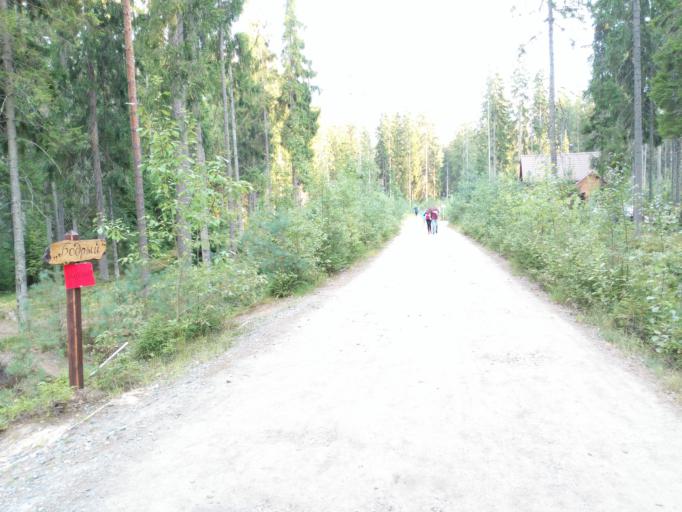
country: RU
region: Leningrad
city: Il'ichevo
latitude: 60.2826
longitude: 29.7463
